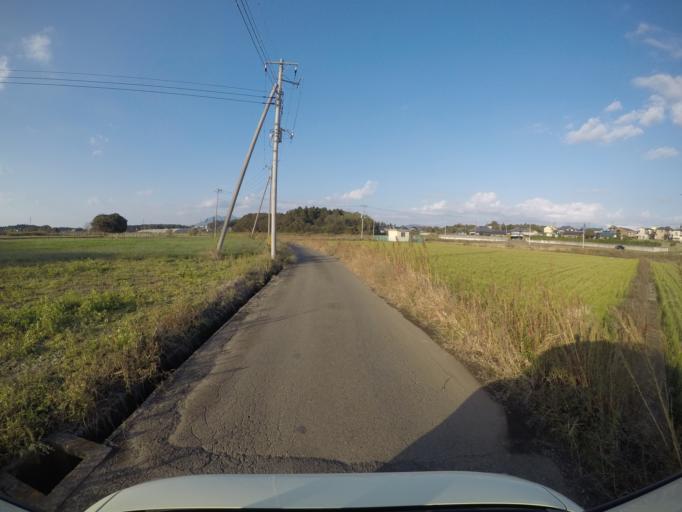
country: JP
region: Ibaraki
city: Naka
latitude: 36.0915
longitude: 140.1226
